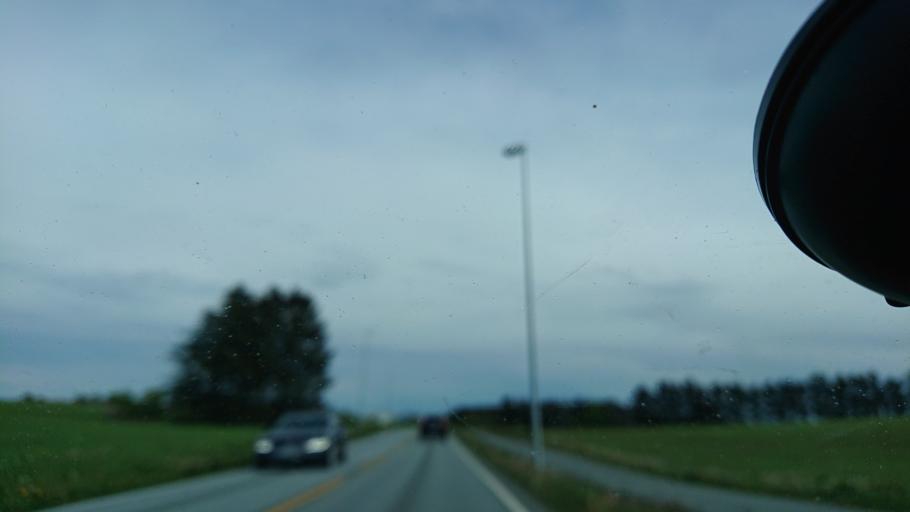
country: NO
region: Rogaland
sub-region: Sola
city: Tananger
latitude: 58.9426
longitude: 5.6012
